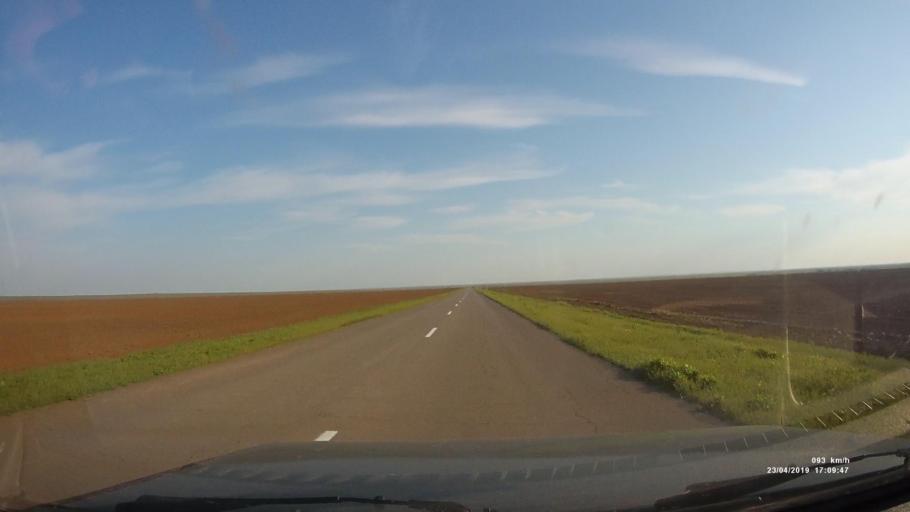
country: RU
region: Kalmykiya
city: Priyutnoye
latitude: 46.2536
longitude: 43.4842
